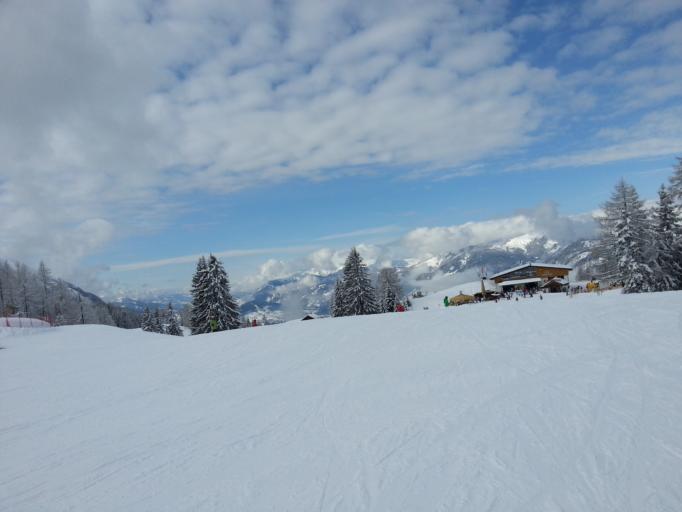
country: AT
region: Salzburg
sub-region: Politischer Bezirk Sankt Johann im Pongau
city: Sankt Johann im Pongau
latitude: 47.3101
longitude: 13.2267
